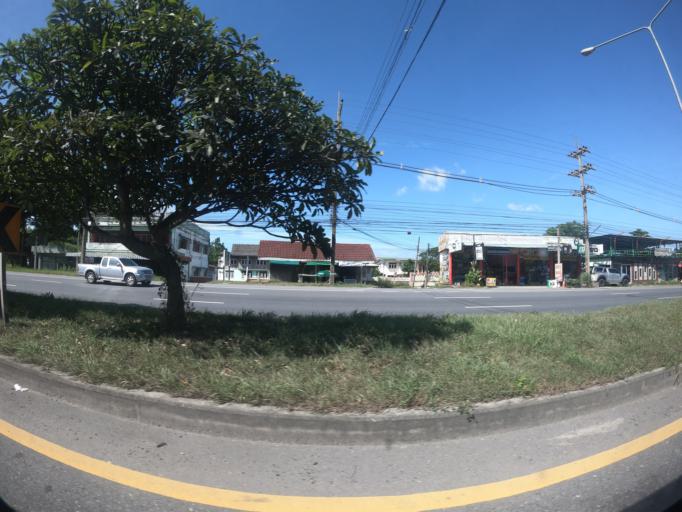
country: TH
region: Nakhon Nayok
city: Ban Na
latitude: 14.2570
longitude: 101.0792
